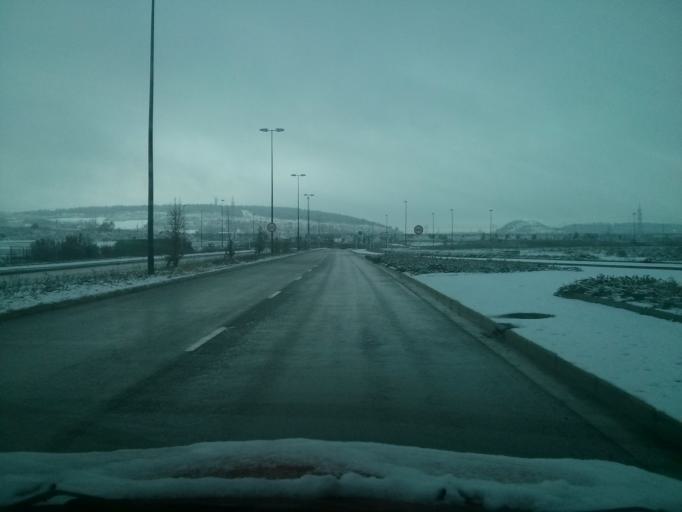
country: ES
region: Castille and Leon
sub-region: Provincia de Burgos
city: Burgos
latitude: 42.3724
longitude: -3.6989
